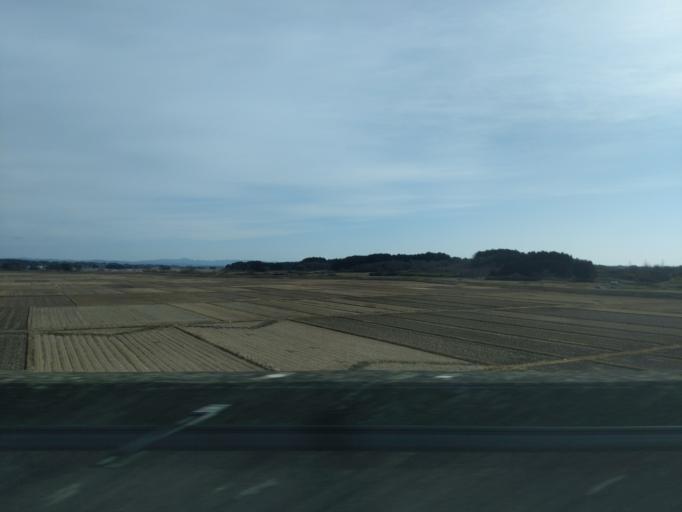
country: JP
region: Miyagi
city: Furukawa
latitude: 38.6511
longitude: 141.0163
